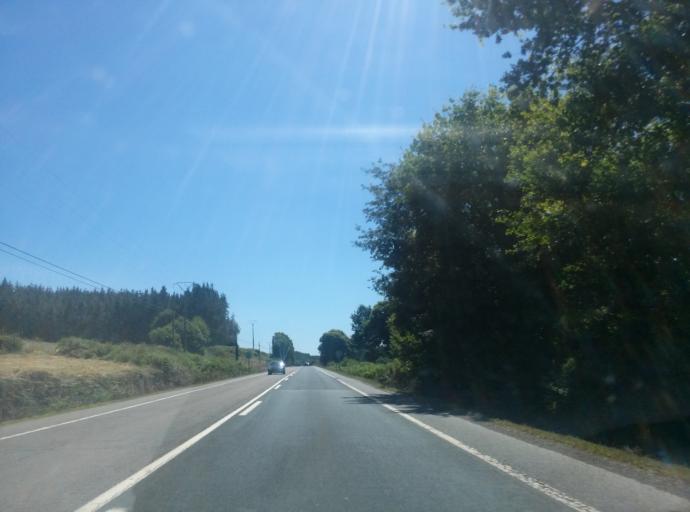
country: ES
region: Galicia
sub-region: Provincia de Lugo
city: Castro de Rei
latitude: 43.1240
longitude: -7.4244
